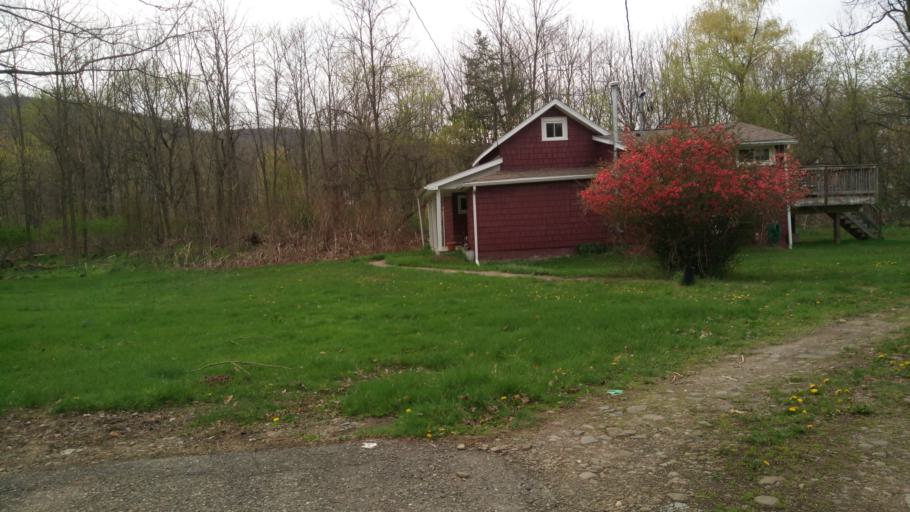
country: US
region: New York
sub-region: Chemung County
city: Southport
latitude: 42.0149
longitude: -76.7299
